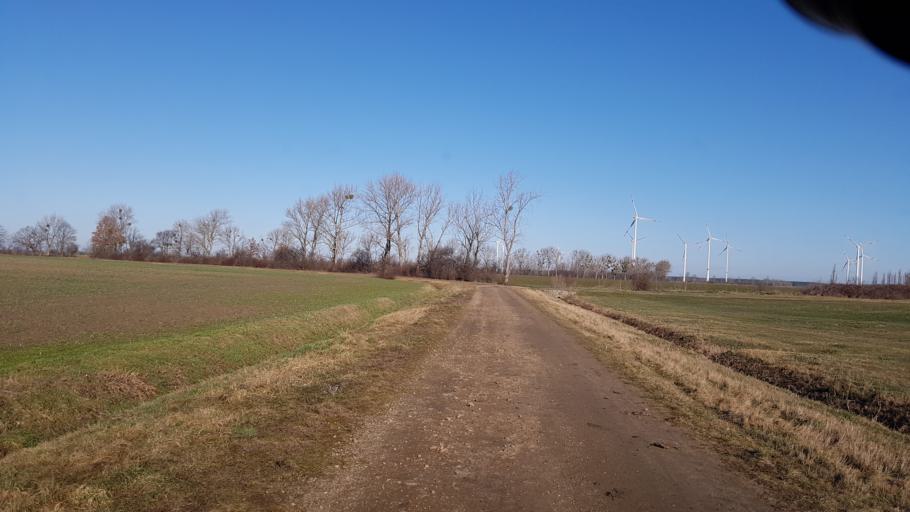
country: DE
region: Brandenburg
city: Muhlberg
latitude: 51.5008
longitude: 13.2234
